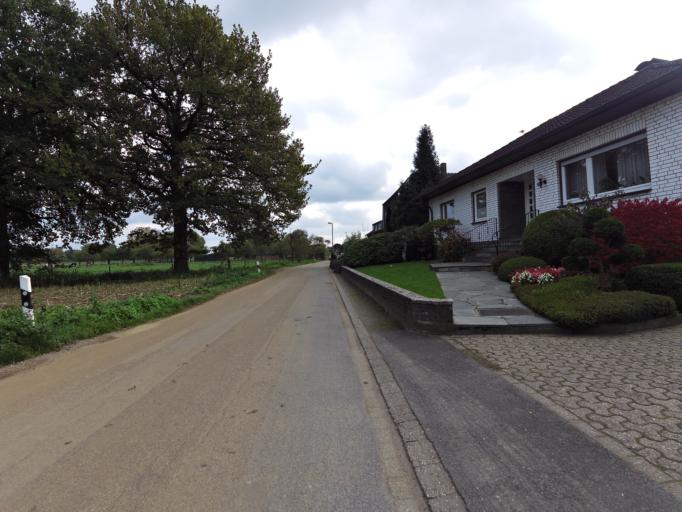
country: DE
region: North Rhine-Westphalia
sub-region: Regierungsbezirk Munster
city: Isselburg
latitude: 51.8303
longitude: 6.4700
